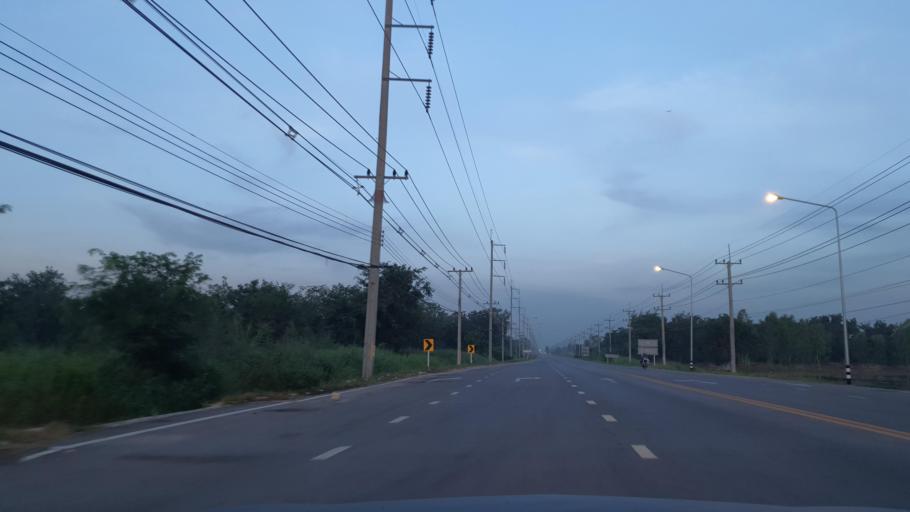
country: TH
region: Nakhon Sawan
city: Kao Liao
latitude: 15.7677
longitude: 99.9804
